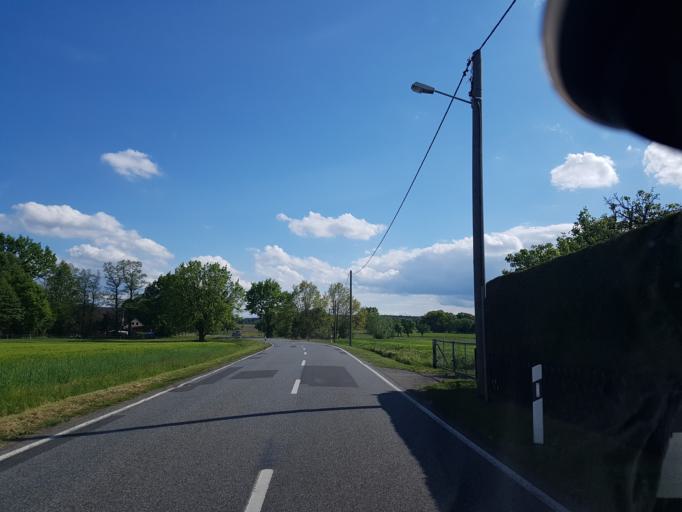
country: DE
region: Brandenburg
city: Drebkau
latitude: 51.6401
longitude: 14.2777
